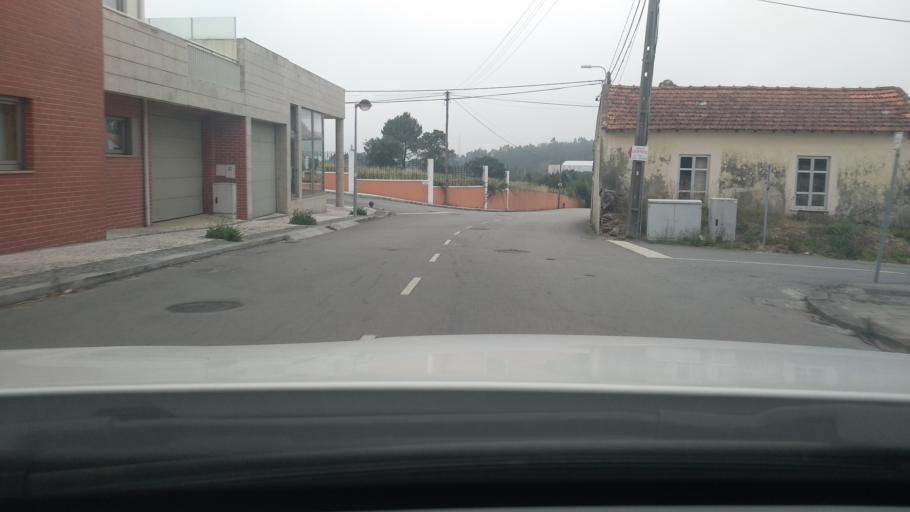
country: PT
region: Aveiro
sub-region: Espinho
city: Silvalde
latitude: 40.9942
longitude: -8.6264
